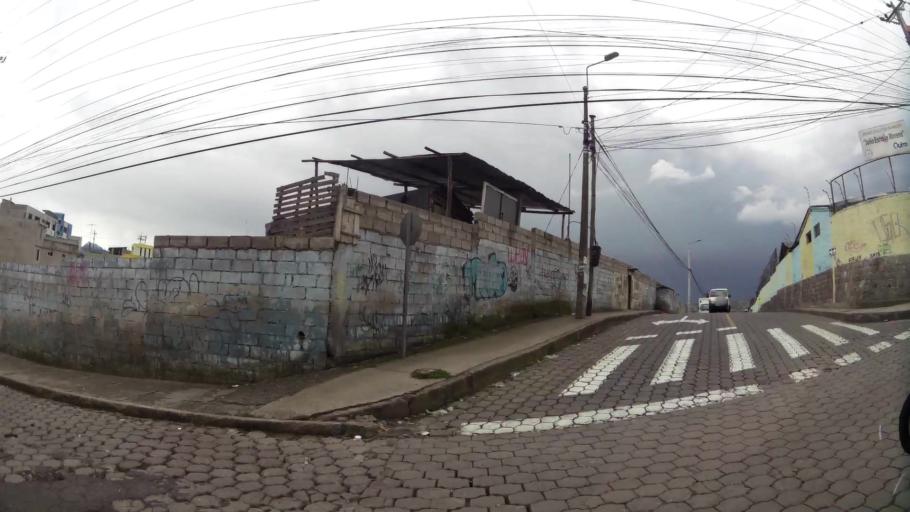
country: EC
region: Pichincha
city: Sangolqui
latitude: -0.3335
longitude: -78.5539
